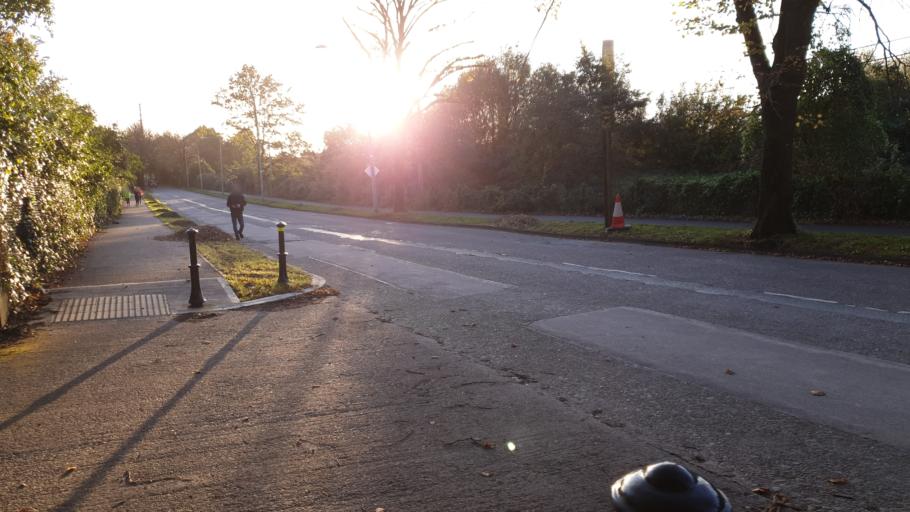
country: IE
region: Munster
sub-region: County Cork
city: Cork
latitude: 51.9007
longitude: -8.4391
